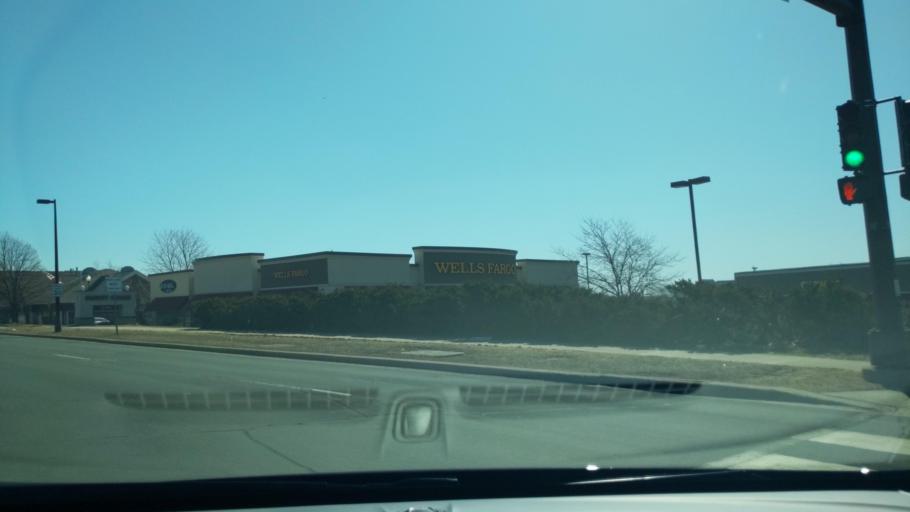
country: US
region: Minnesota
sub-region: Carver County
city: Chanhassen
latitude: 44.8623
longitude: -93.5401
